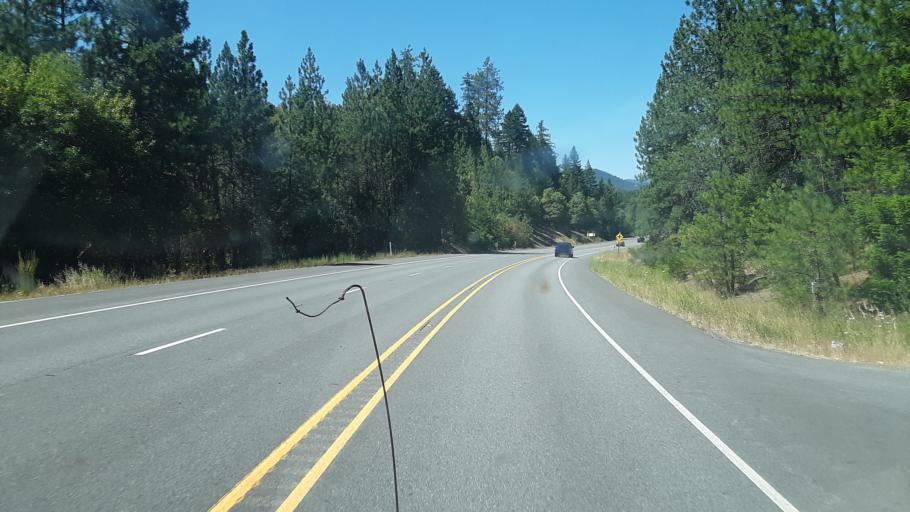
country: US
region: Oregon
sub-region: Josephine County
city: Cave Junction
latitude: 42.2678
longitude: -123.6197
